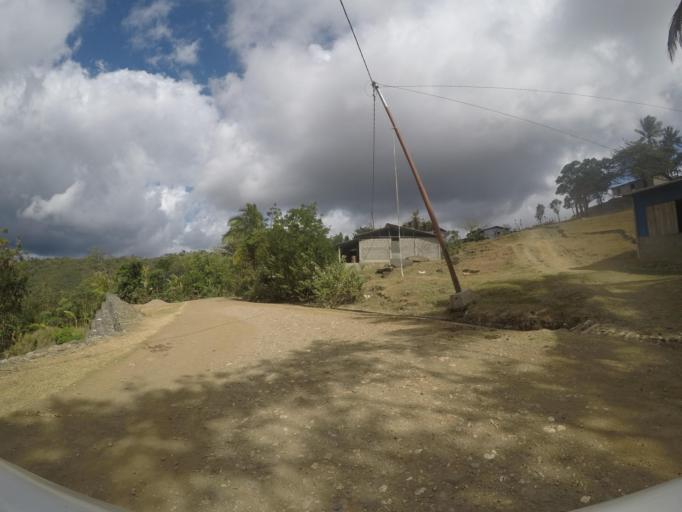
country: TL
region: Lautem
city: Lospalos
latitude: -8.5455
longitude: 126.8347
